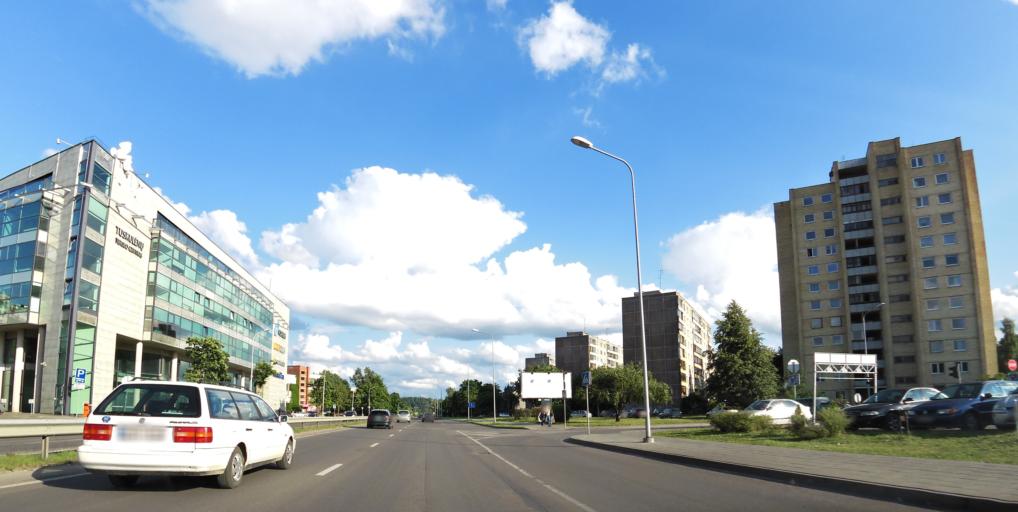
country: LT
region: Vilnius County
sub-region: Vilnius
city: Vilnius
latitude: 54.7024
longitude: 25.2898
